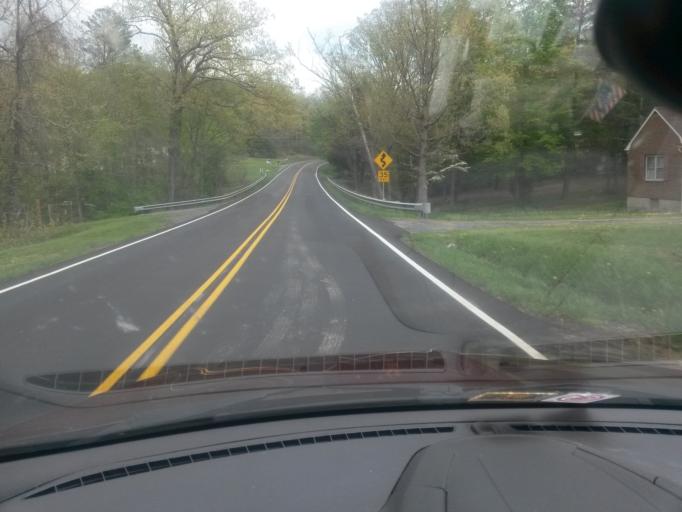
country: US
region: Virginia
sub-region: City of Covington
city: Covington
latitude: 37.8005
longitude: -80.0154
